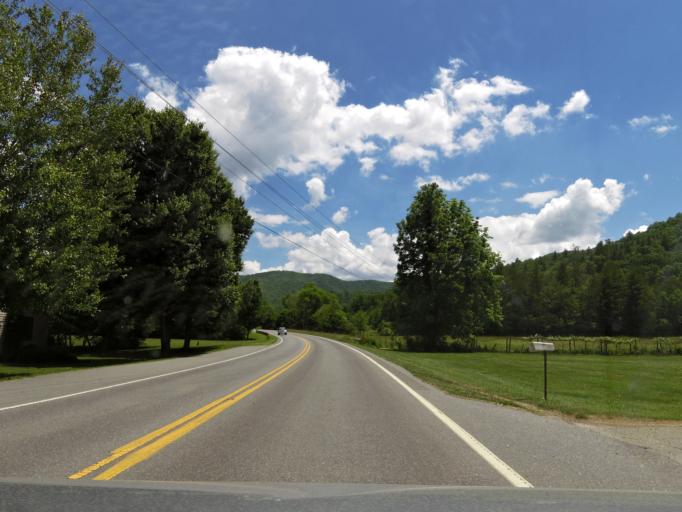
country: US
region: North Carolina
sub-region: Graham County
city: Robbinsville
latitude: 35.2983
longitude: -83.7942
